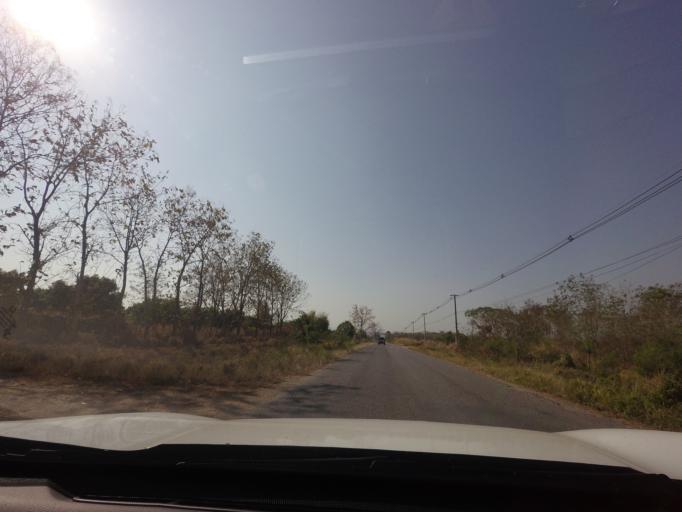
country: TH
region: Nakhon Ratchasima
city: Pak Chong
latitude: 14.6251
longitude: 101.4855
